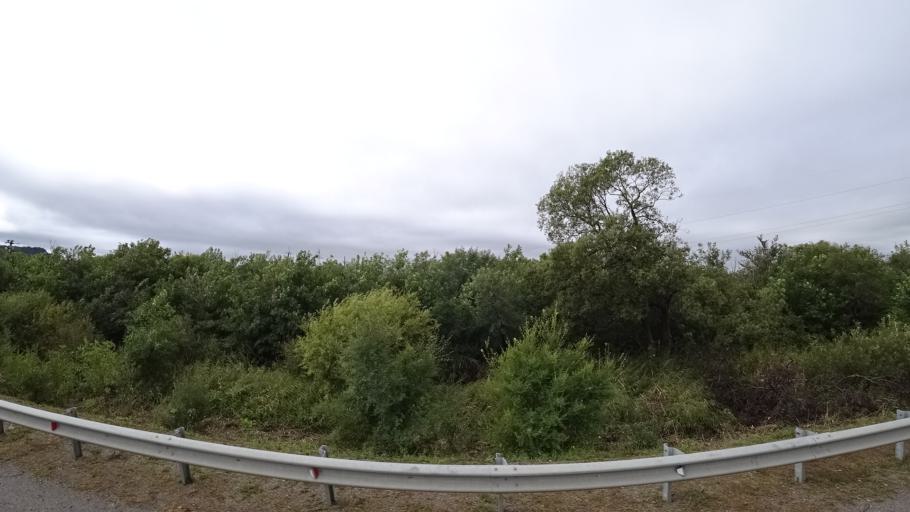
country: RU
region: Primorskiy
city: Monastyrishche
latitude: 44.1785
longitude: 132.4414
